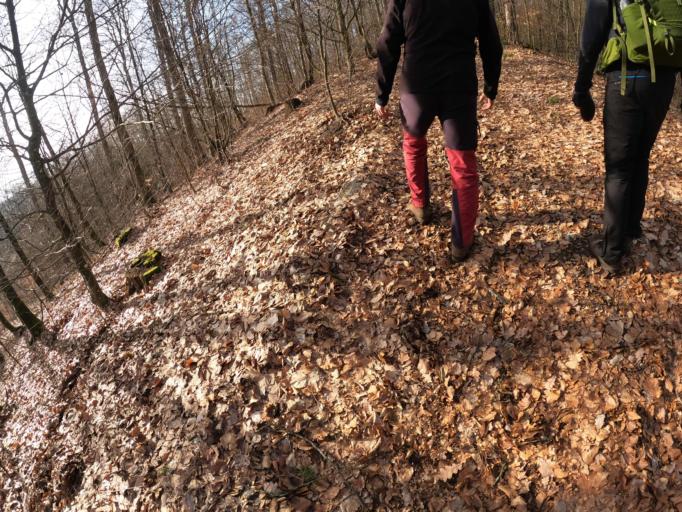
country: PL
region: West Pomeranian Voivodeship
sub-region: Powiat koszalinski
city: Polanow
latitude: 54.1204
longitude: 16.7019
